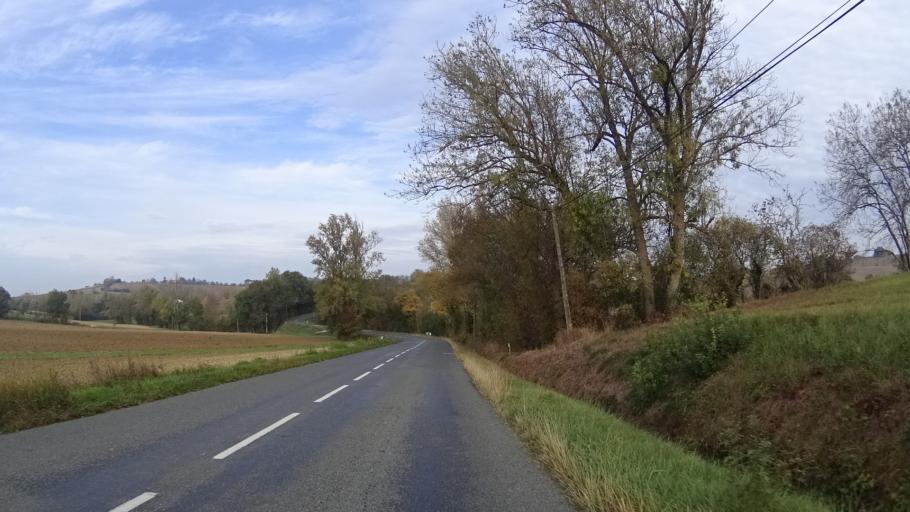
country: FR
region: Aquitaine
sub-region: Departement du Lot-et-Garonne
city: Laplume
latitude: 44.1036
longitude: 0.5503
